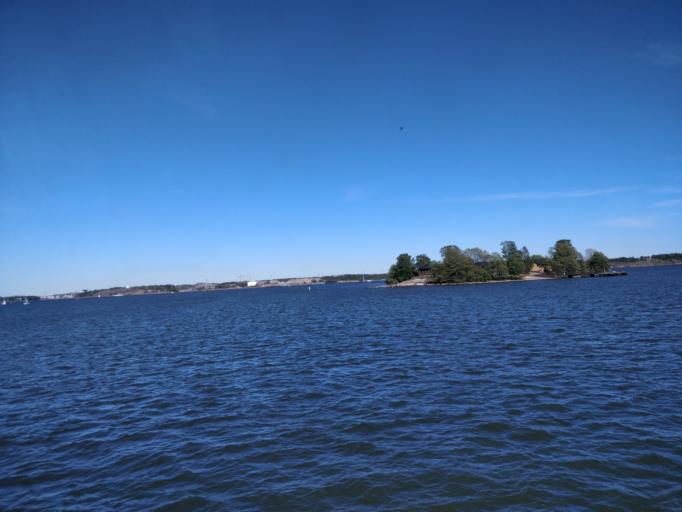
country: FI
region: Uusimaa
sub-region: Helsinki
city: Helsinki
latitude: 60.1535
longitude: 24.9833
